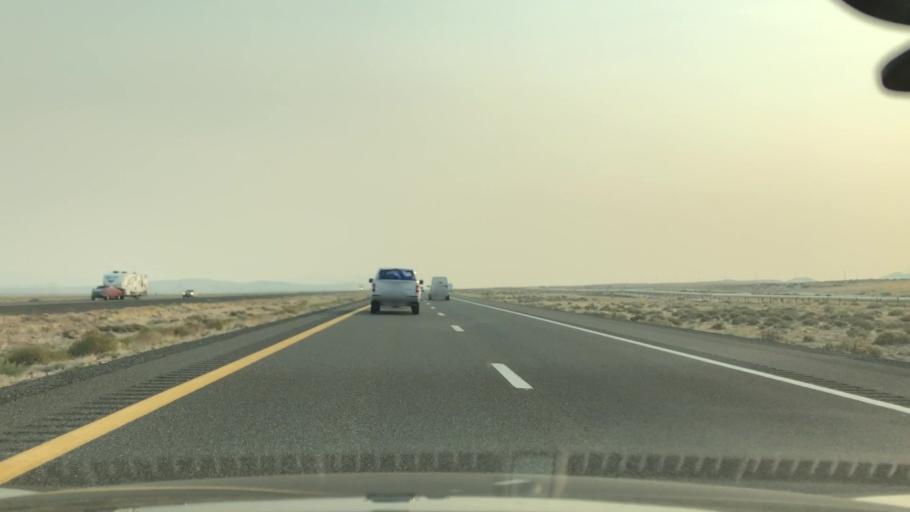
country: US
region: Nevada
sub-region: Lyon County
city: Fernley
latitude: 39.8060
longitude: -119.0072
